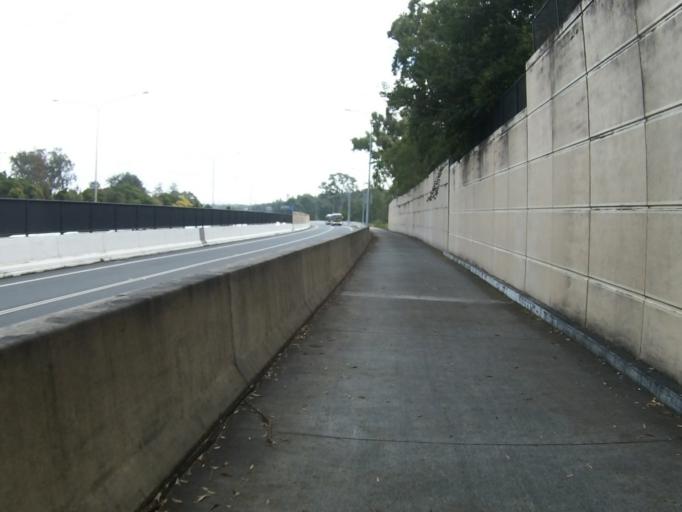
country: AU
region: Queensland
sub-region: Brisbane
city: Greenslopes
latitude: -27.5185
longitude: 153.0510
